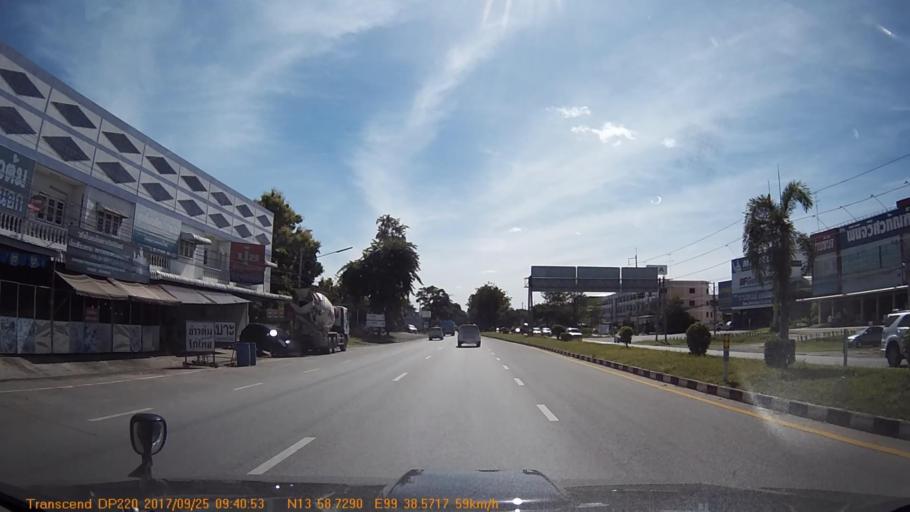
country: TH
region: Kanchanaburi
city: Tha Muang
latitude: 13.9788
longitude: 99.6431
